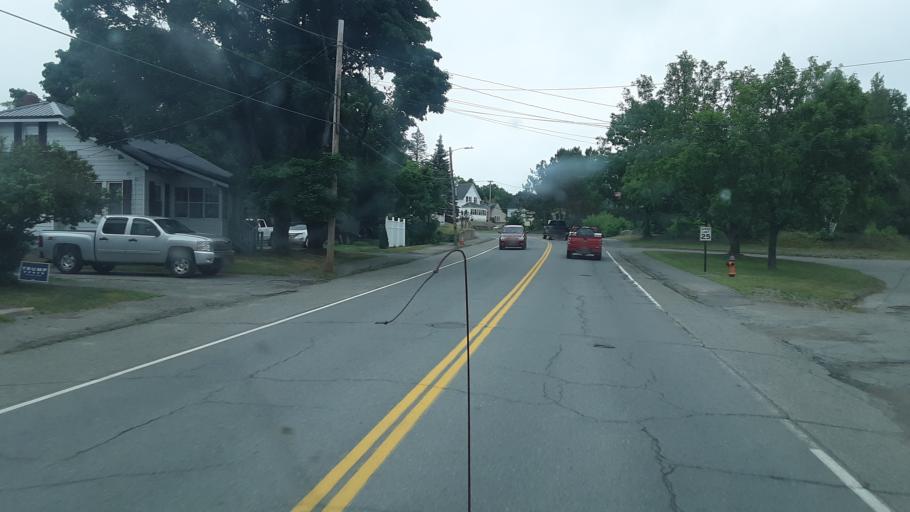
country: US
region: Maine
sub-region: Penobscot County
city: Millinocket
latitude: 45.6619
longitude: -68.7141
